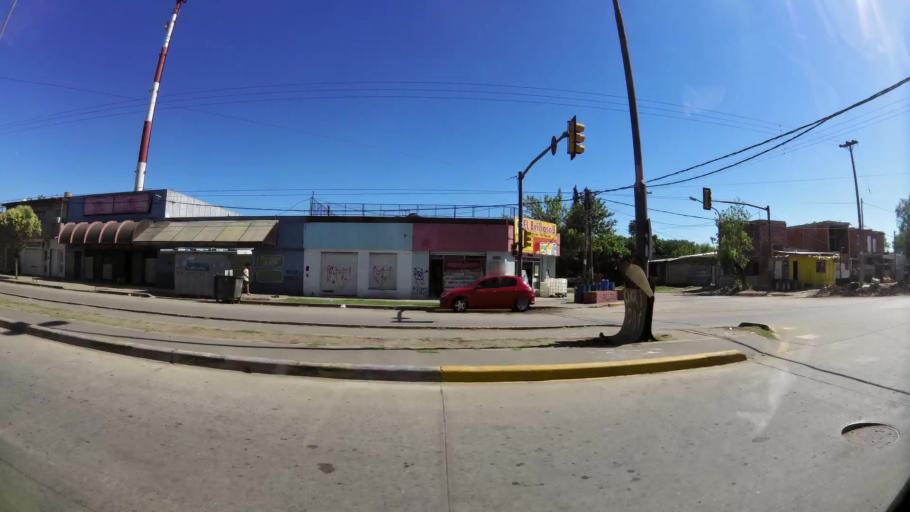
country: AR
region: Santa Fe
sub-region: Departamento de Rosario
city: Rosario
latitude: -32.9706
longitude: -60.6927
